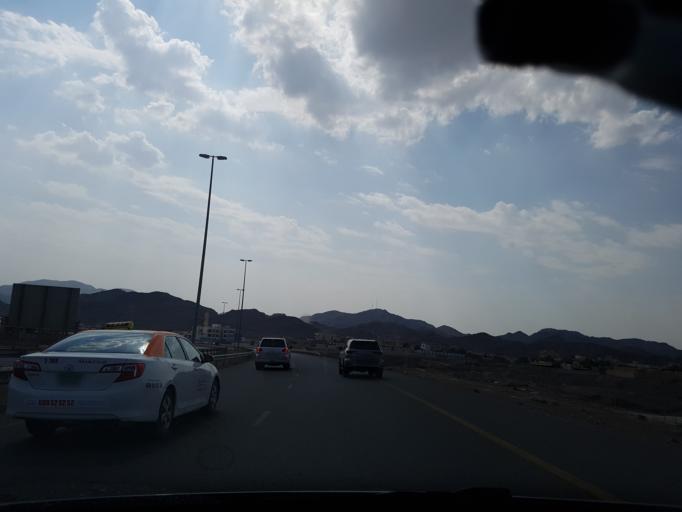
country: AE
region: Al Fujayrah
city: Dibba Al-Fujairah
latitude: 25.5138
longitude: 56.0770
